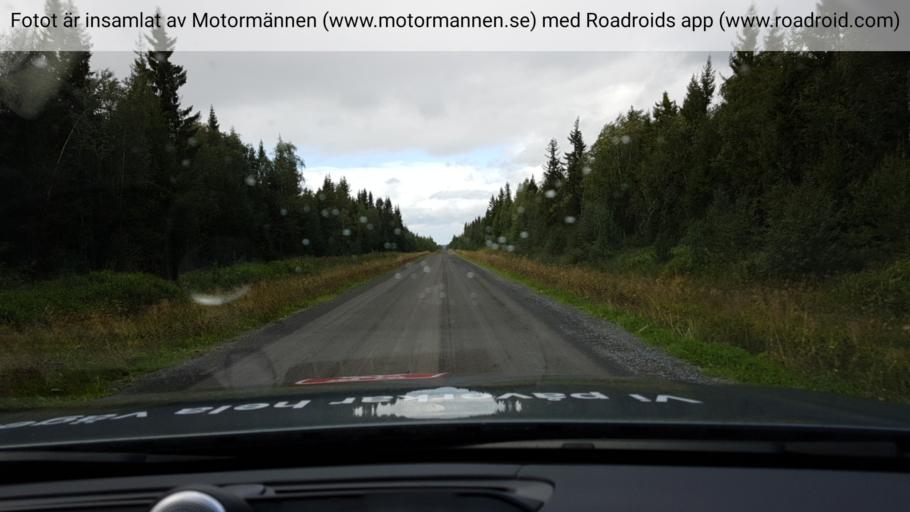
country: SE
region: Jaemtland
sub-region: OEstersunds Kommun
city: Lit
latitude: 63.6552
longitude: 14.9279
